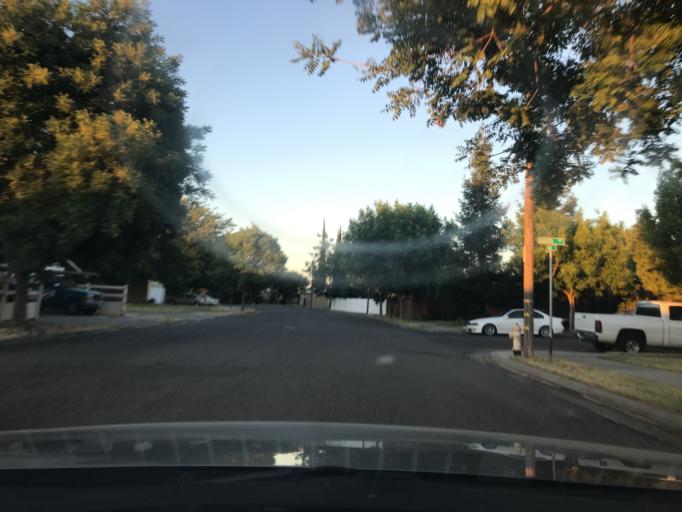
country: US
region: California
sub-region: Merced County
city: Atwater
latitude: 37.3519
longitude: -120.5995
